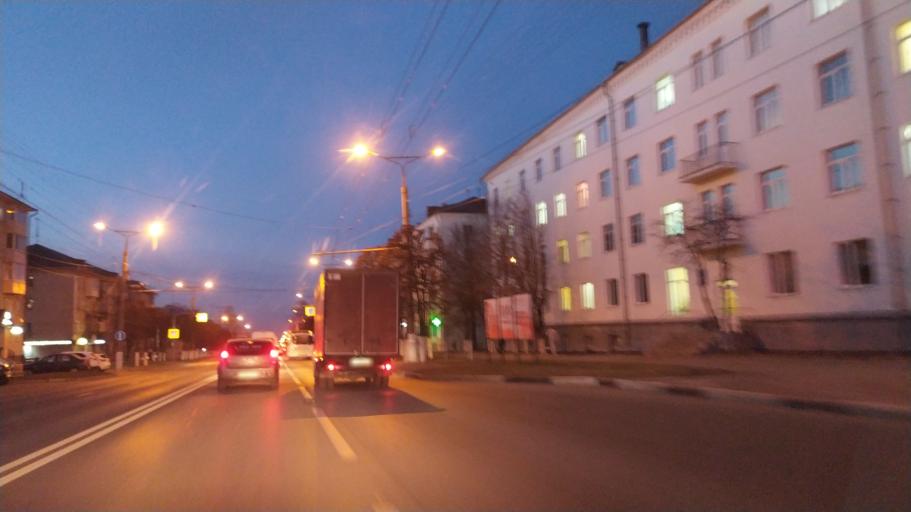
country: RU
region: Chuvashia
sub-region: Cheboksarskiy Rayon
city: Cheboksary
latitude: 56.1190
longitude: 47.2568
